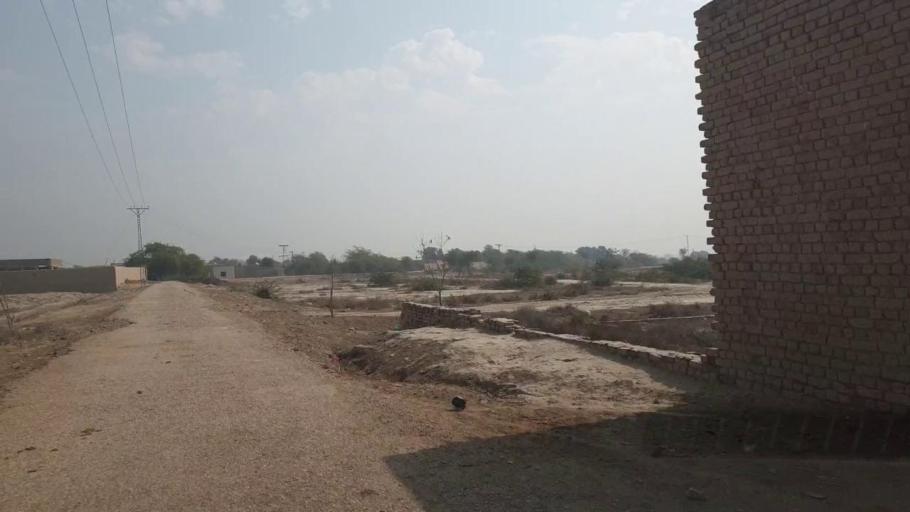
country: PK
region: Sindh
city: Hala
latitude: 25.7945
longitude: 68.4196
